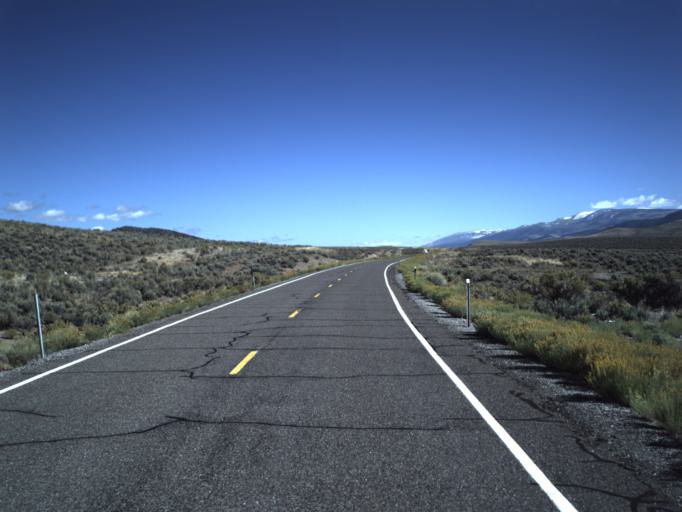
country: US
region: Utah
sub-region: Piute County
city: Junction
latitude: 38.3152
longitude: -111.9665
